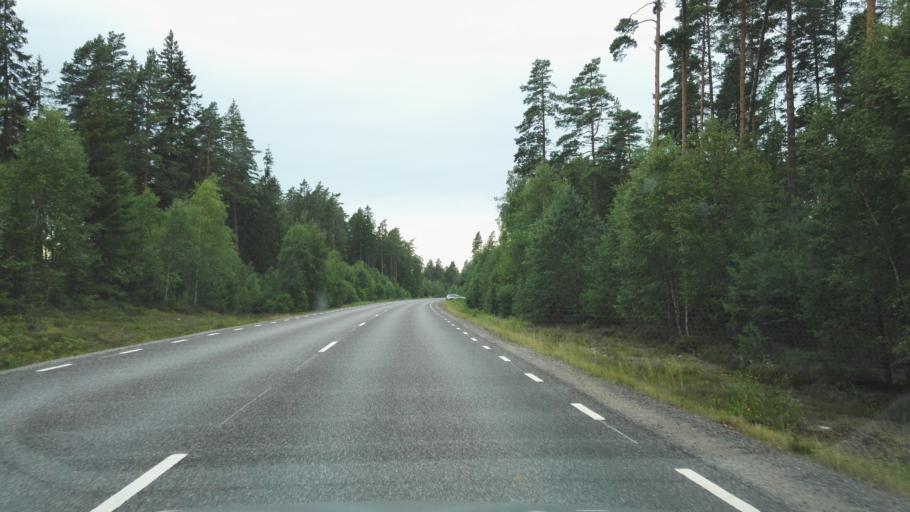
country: SE
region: Kronoberg
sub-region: Vaxjo Kommun
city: Braas
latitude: 57.0543
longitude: 15.0555
